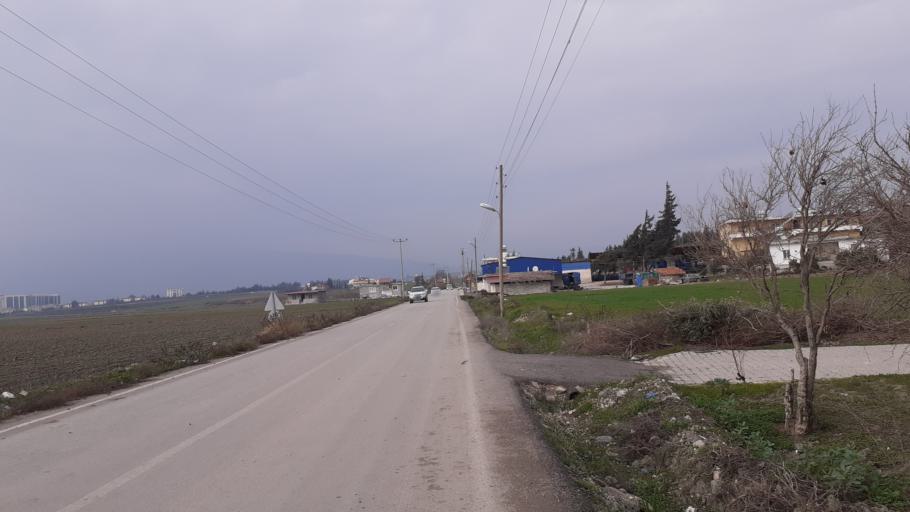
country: TR
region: Hatay
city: Kastal
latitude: 36.2623
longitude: 36.2426
